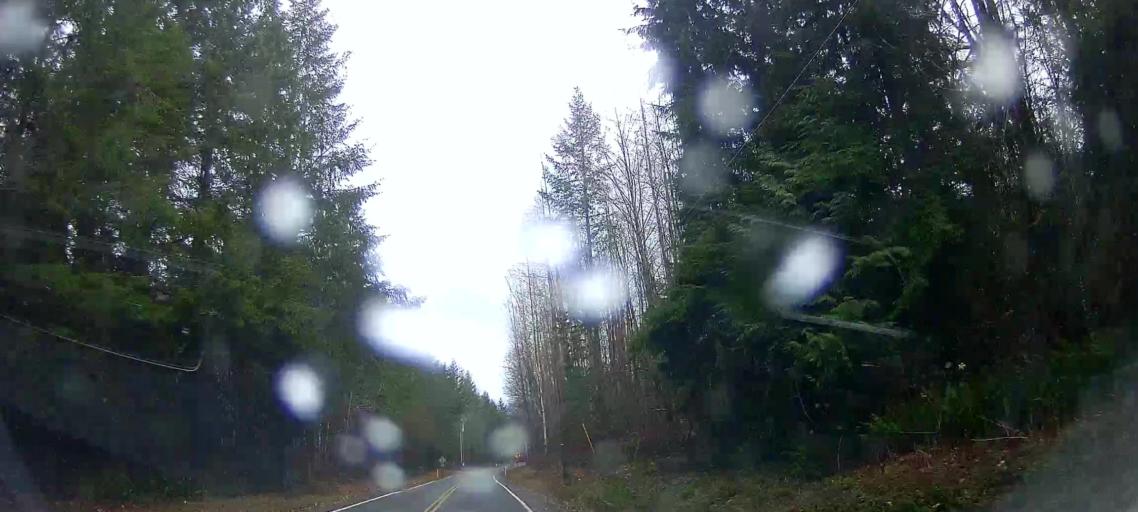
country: US
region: Washington
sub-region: Skagit County
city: Clear Lake
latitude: 48.4774
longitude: -122.1414
